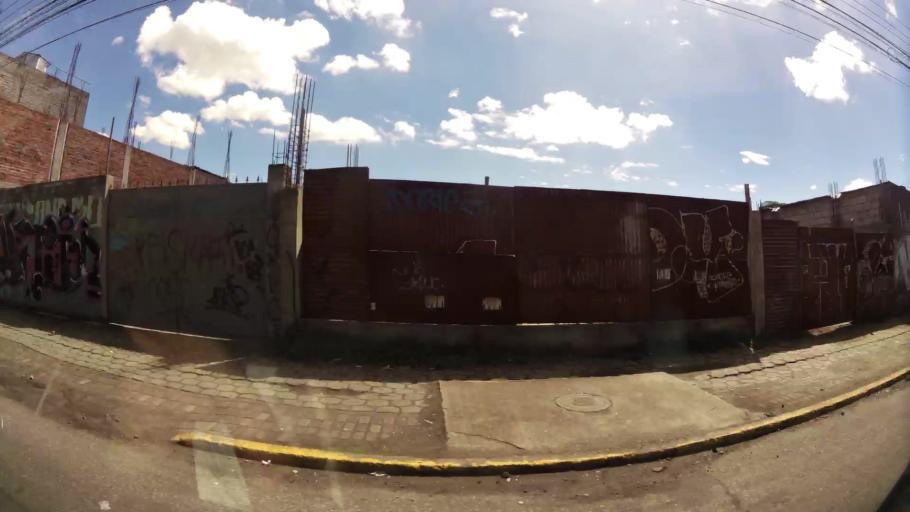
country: EC
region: Pichincha
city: Quito
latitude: -0.2989
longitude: -78.5459
